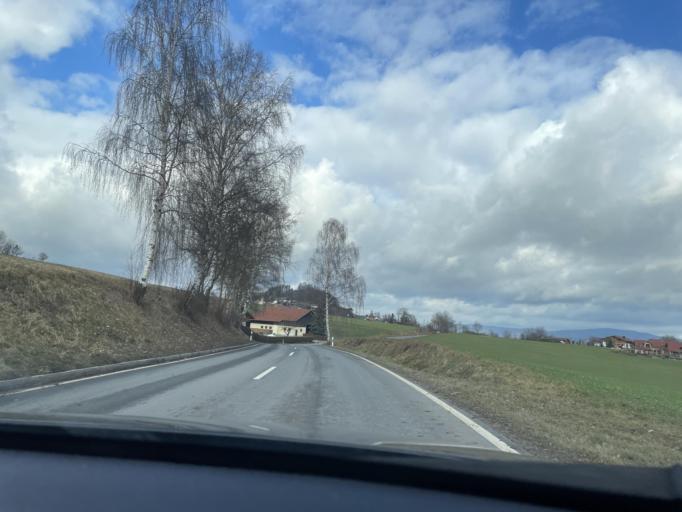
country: DE
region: Bavaria
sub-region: Upper Palatinate
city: Runding
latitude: 49.2088
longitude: 12.7698
